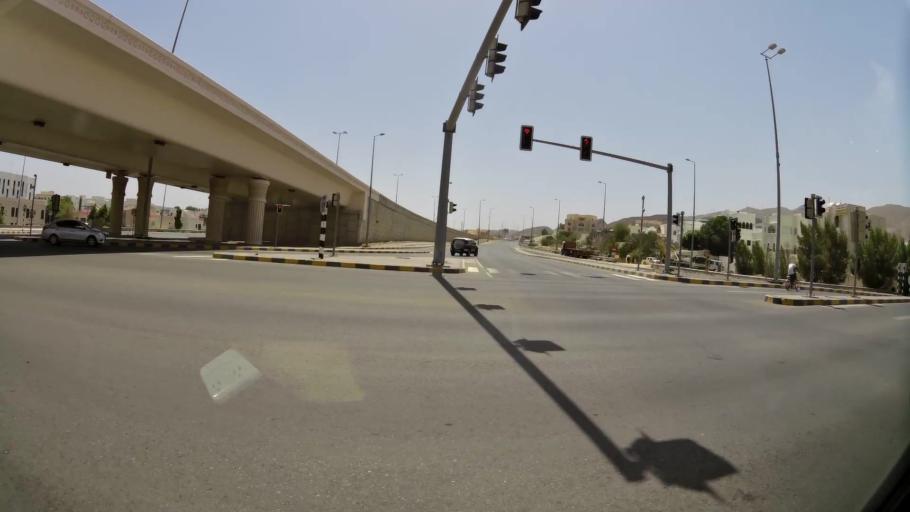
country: OM
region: Muhafazat Masqat
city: Bawshar
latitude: 23.5905
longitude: 58.4473
